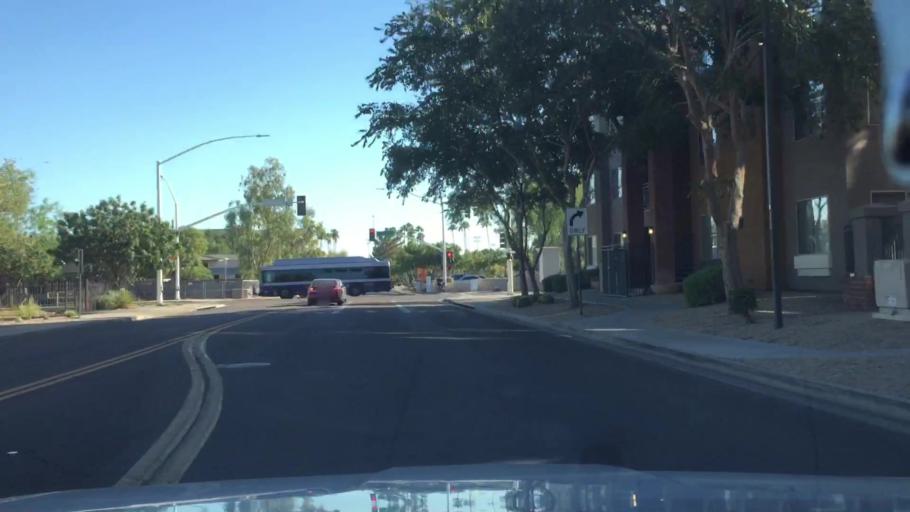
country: US
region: Arizona
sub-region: Maricopa County
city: Scottsdale
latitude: 33.4956
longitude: -111.9197
